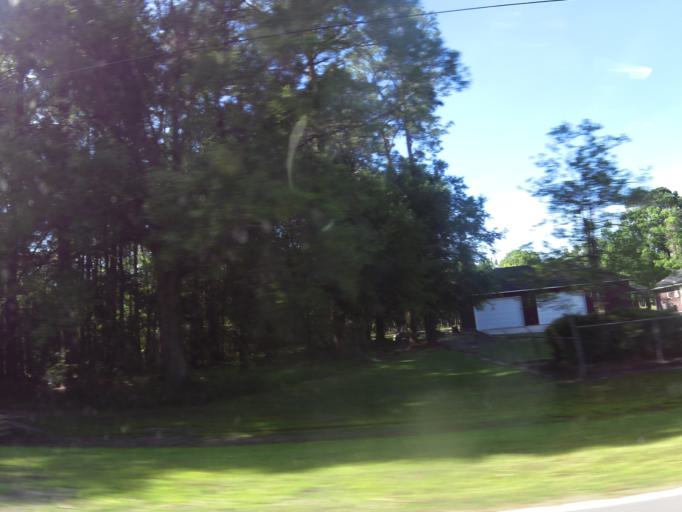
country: US
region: Florida
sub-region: Nassau County
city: Callahan
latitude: 30.5624
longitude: -81.8052
